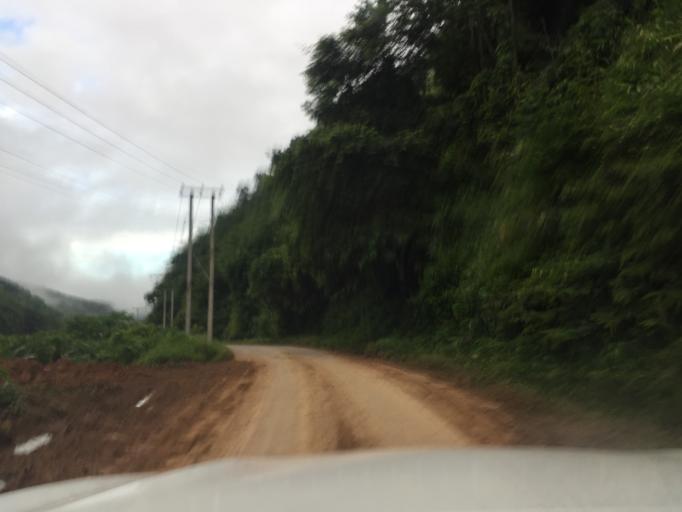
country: LA
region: Phongsali
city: Khoa
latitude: 21.0779
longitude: 102.3771
